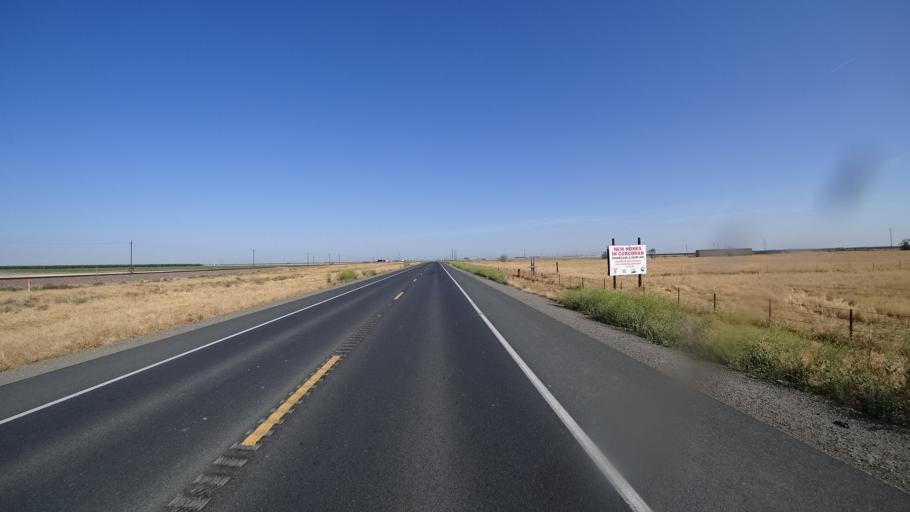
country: US
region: California
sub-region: Kings County
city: Corcoran
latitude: 36.1345
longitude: -119.5826
